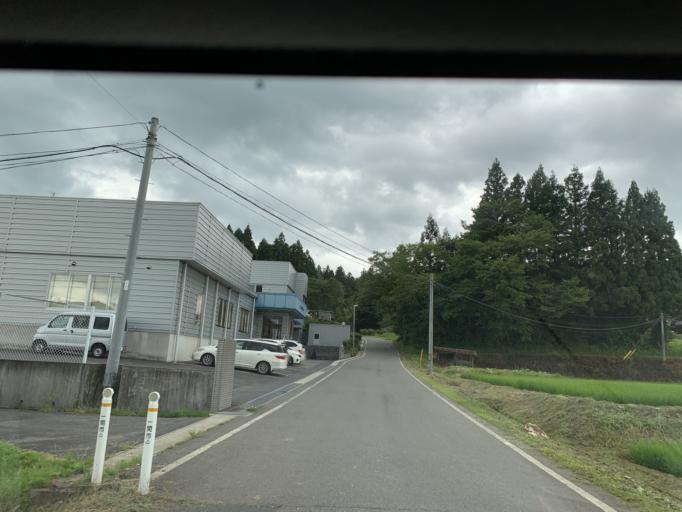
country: JP
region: Iwate
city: Ichinoseki
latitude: 38.9447
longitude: 141.0408
